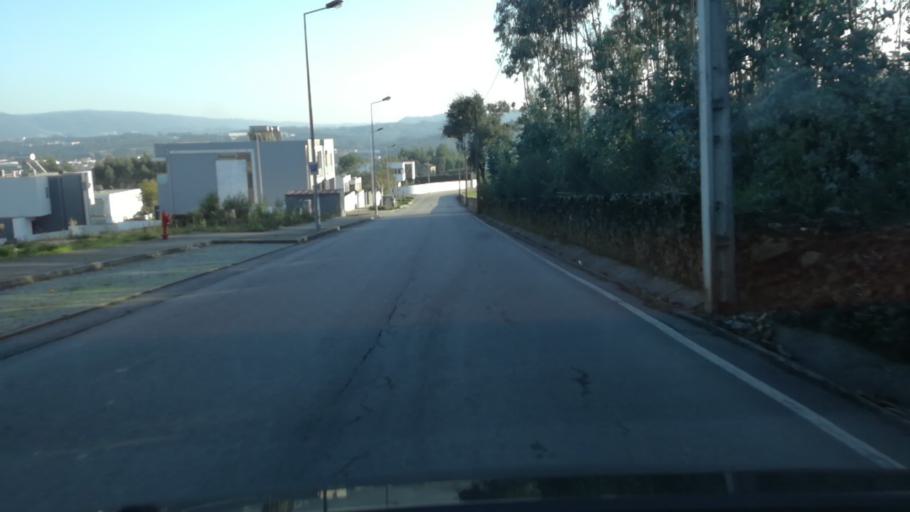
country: PT
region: Braga
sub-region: Vila Nova de Famalicao
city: Ferreiros
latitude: 41.3608
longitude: -8.5312
